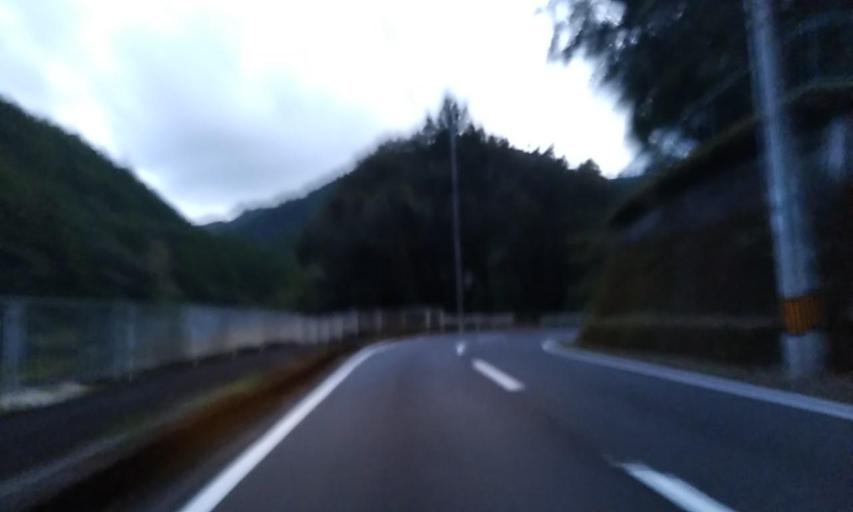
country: JP
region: Wakayama
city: Shingu
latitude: 33.7340
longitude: 135.9305
